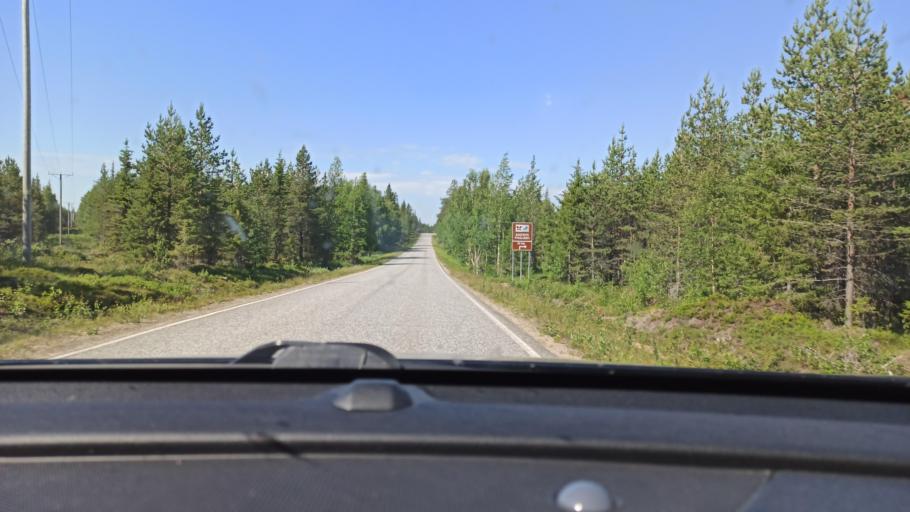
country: FI
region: Lapland
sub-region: Tunturi-Lappi
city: Kolari
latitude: 67.6839
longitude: 24.1215
